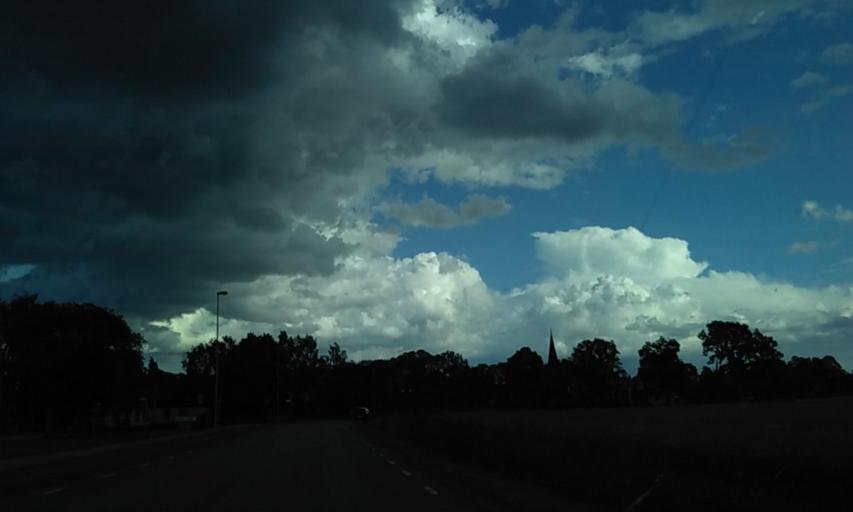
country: SE
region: Vaestra Goetaland
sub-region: Lidkopings Kommun
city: Lidkoping
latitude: 58.5103
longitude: 13.0037
